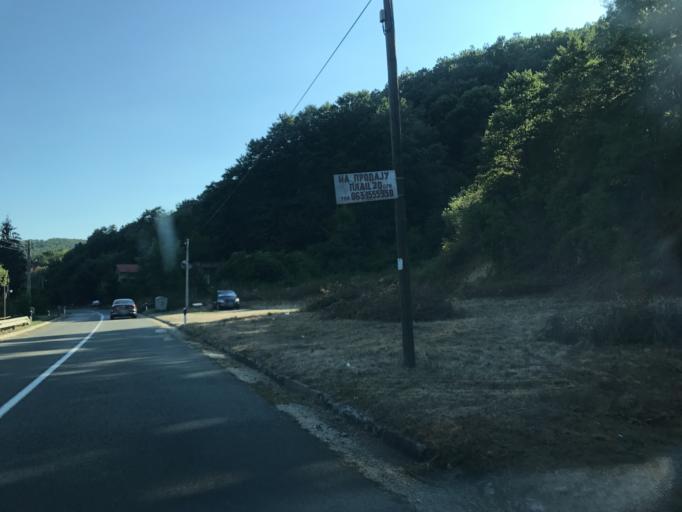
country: RO
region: Mehedinti
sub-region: Comuna Svinita
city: Svinita
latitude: 44.4588
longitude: 22.1694
